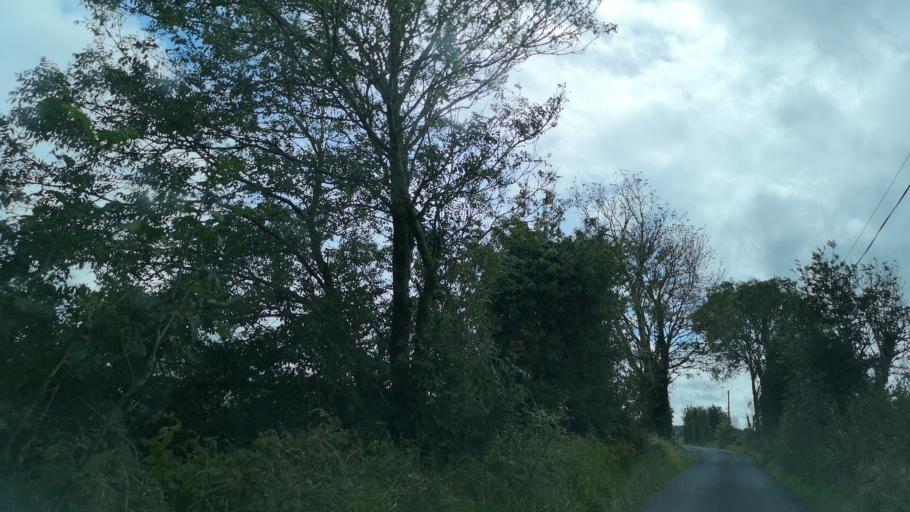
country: IE
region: Connaught
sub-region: County Galway
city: Athenry
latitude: 53.2749
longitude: -8.6724
